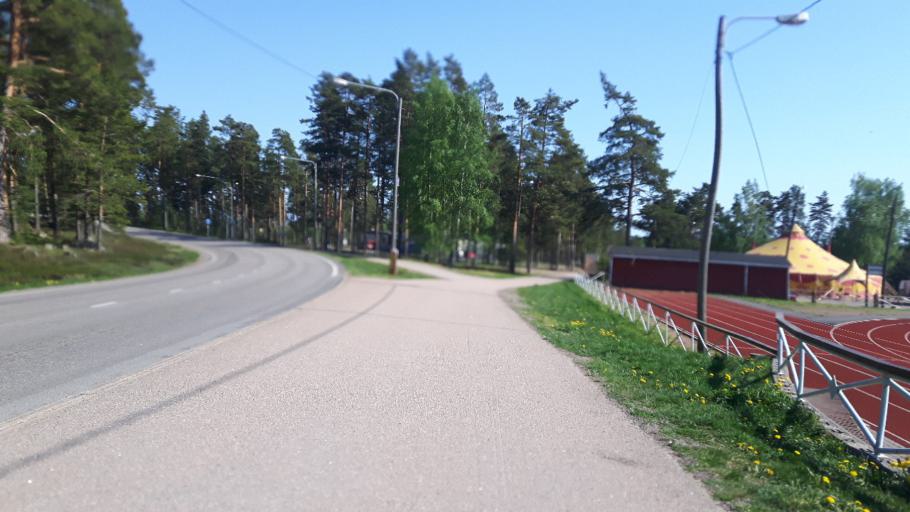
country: FI
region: Kymenlaakso
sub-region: Kotka-Hamina
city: Broby
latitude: 60.4881
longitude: 26.7481
